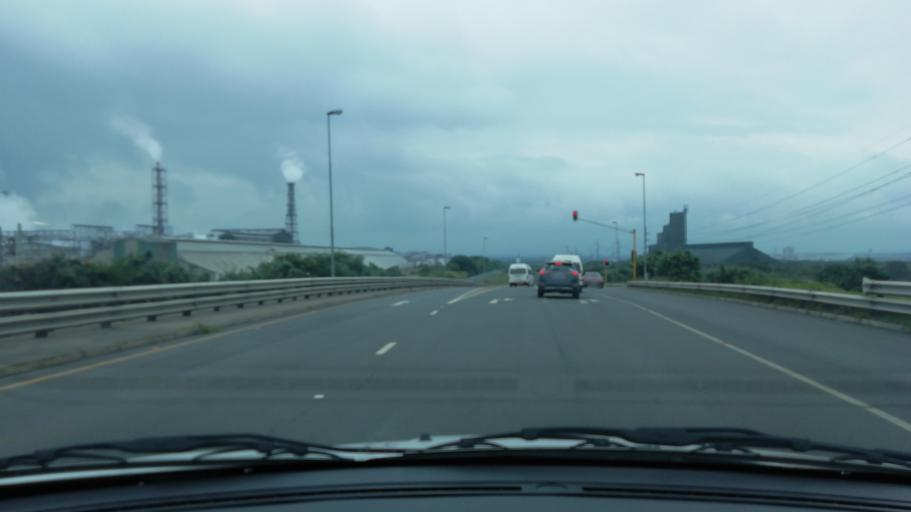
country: ZA
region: KwaZulu-Natal
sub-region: uThungulu District Municipality
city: Richards Bay
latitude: -28.7708
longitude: 32.0341
